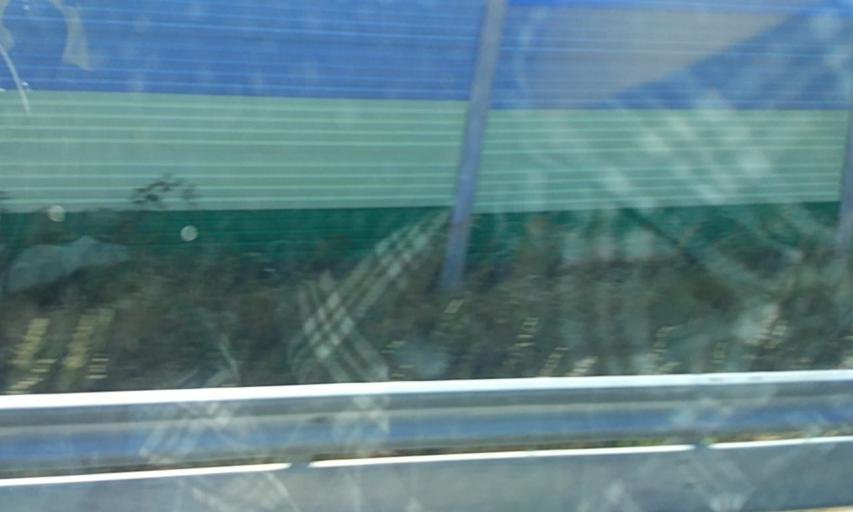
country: PT
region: Braganca
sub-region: Macedo de Cavaleiros
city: Macedo de Cavaleiros
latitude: 41.6397
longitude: -6.8407
